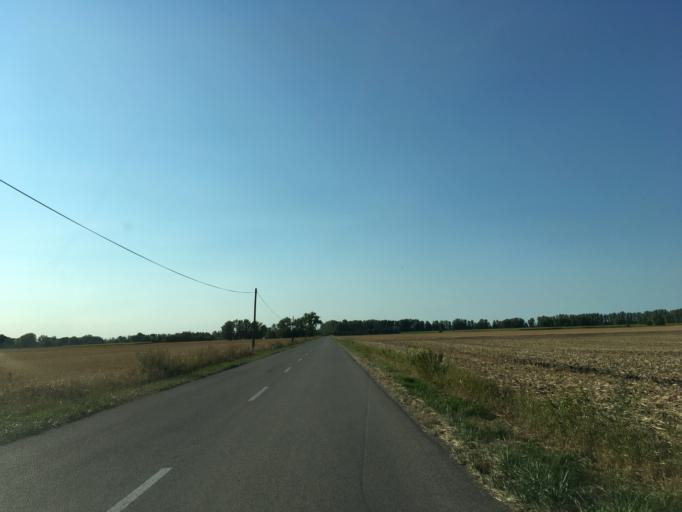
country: SK
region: Nitriansky
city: Kolarovo
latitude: 47.8791
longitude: 17.9114
